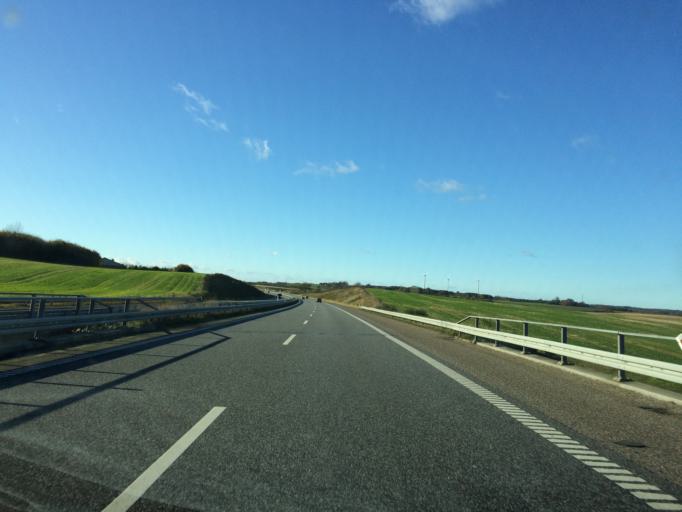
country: DK
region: Central Jutland
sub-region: Hedensted Kommune
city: Torring
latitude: 55.8318
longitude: 9.5120
